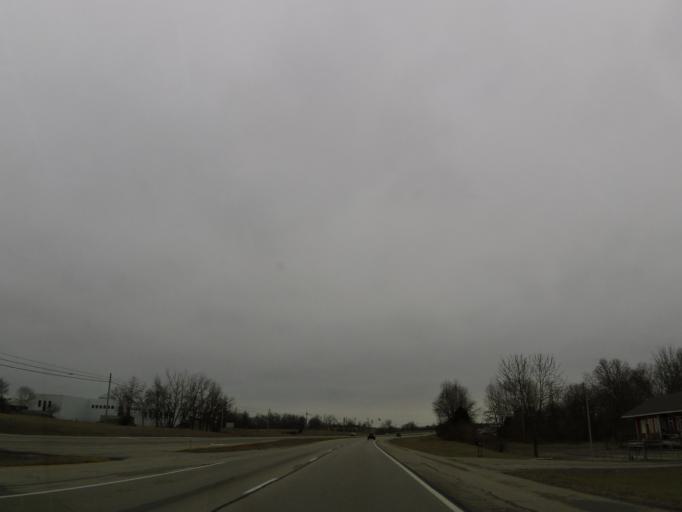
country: US
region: Kentucky
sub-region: Anderson County
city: Lawrenceburg
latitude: 38.0770
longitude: -84.9174
